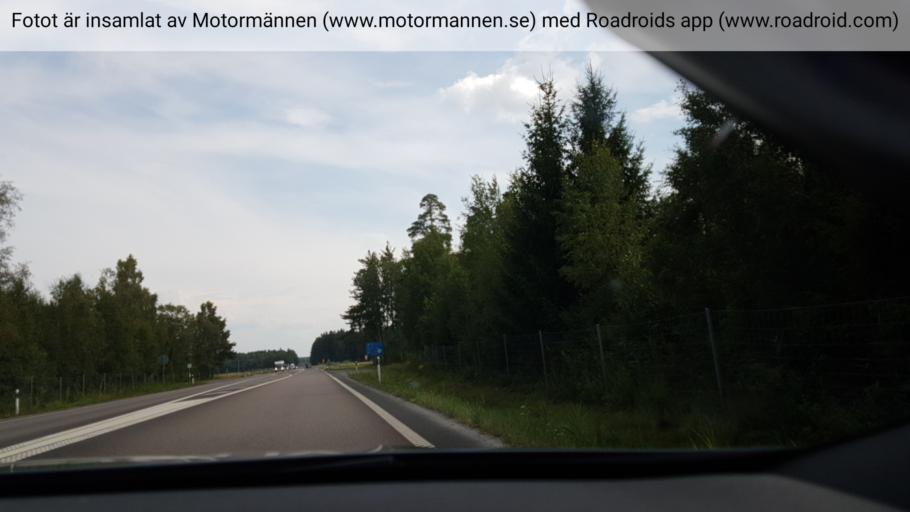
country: SE
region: Vaestra Goetaland
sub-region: Lidkopings Kommun
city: Vinninga
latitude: 58.4642
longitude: 13.2213
